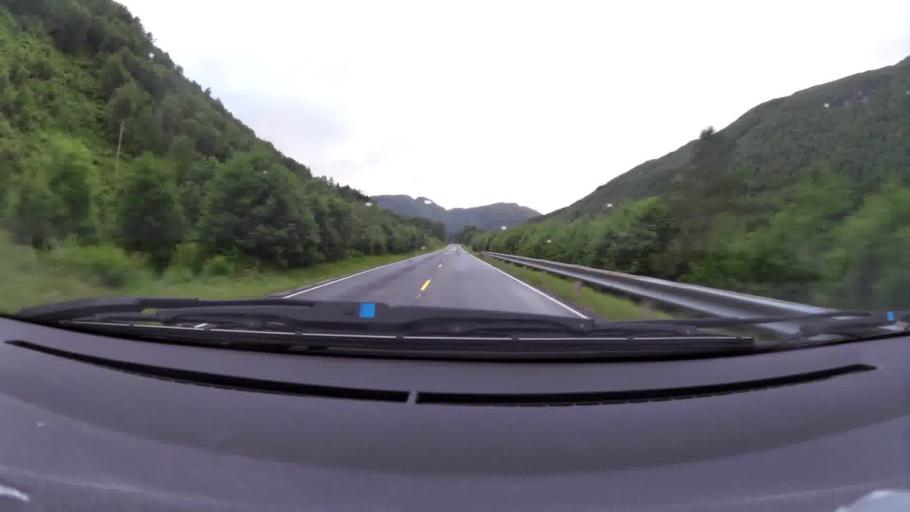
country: NO
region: More og Romsdal
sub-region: Molde
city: Molde
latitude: 62.7965
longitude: 7.2853
